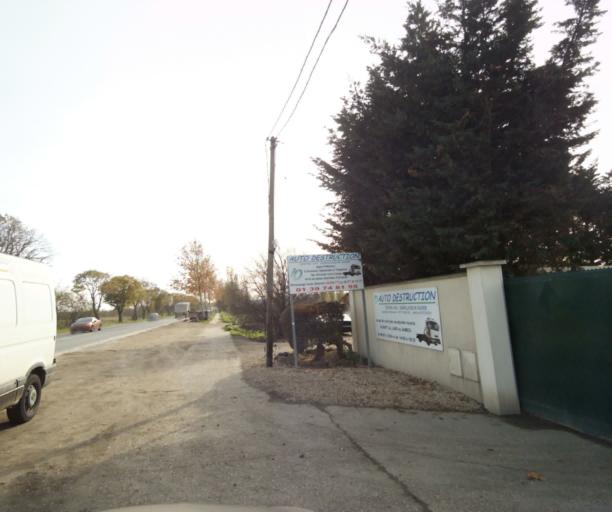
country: FR
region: Ile-de-France
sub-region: Departement des Yvelines
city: Carrieres-sous-Poissy
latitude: 48.9529
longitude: 2.0218
